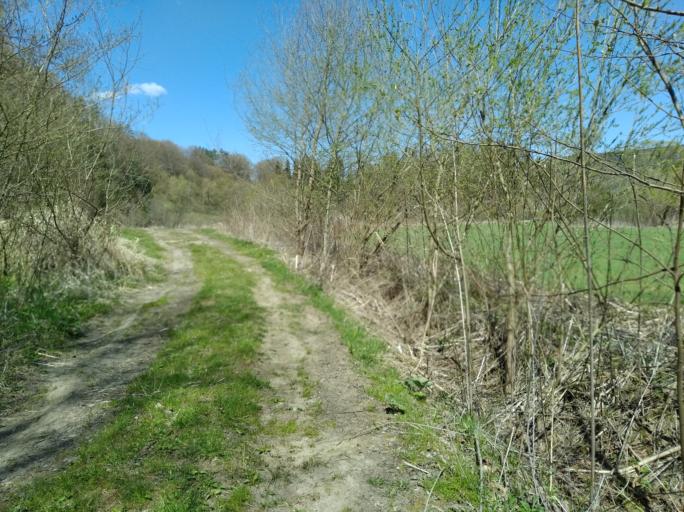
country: PL
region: Subcarpathian Voivodeship
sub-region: Powiat brzozowski
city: Dydnia
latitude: 49.6880
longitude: 22.2373
